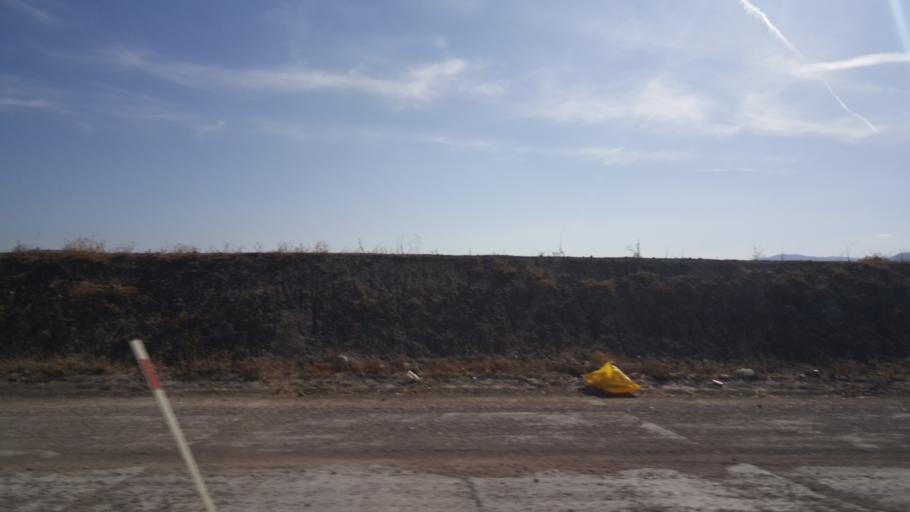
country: TR
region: Ankara
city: Yenice
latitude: 39.3806
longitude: 32.7770
